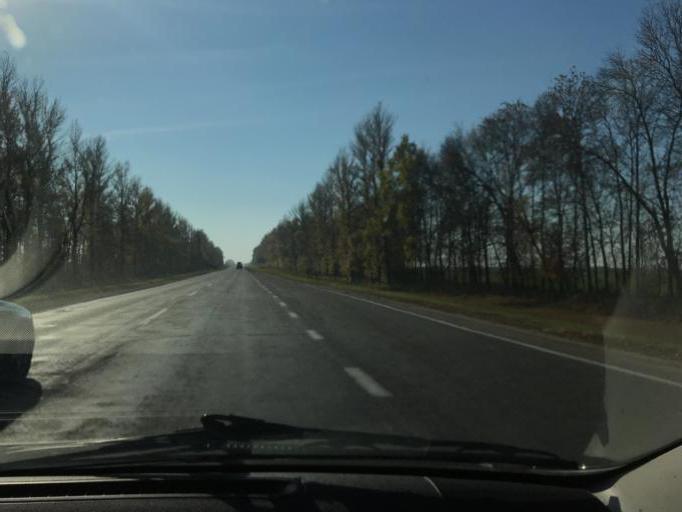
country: BY
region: Minsk
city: Salihorsk
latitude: 52.9009
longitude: 27.4759
